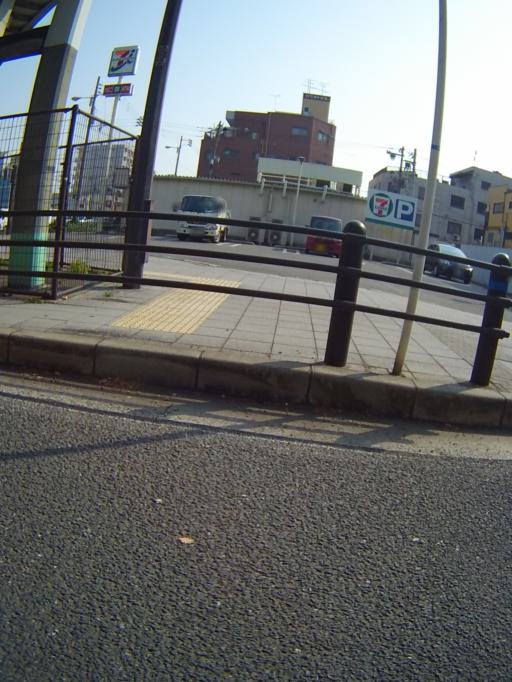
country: JP
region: Osaka
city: Osaka-shi
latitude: 34.6565
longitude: 135.4733
